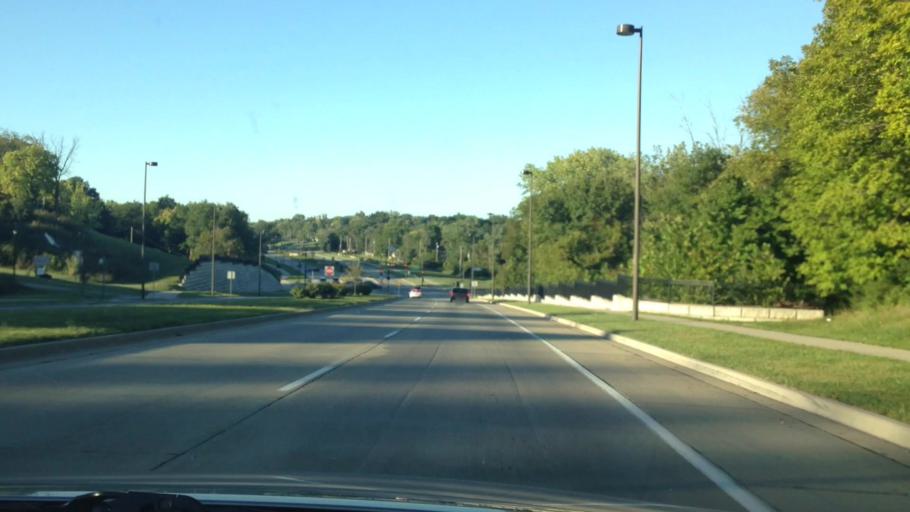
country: US
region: Missouri
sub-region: Clay County
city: North Kansas City
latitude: 39.1600
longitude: -94.5331
